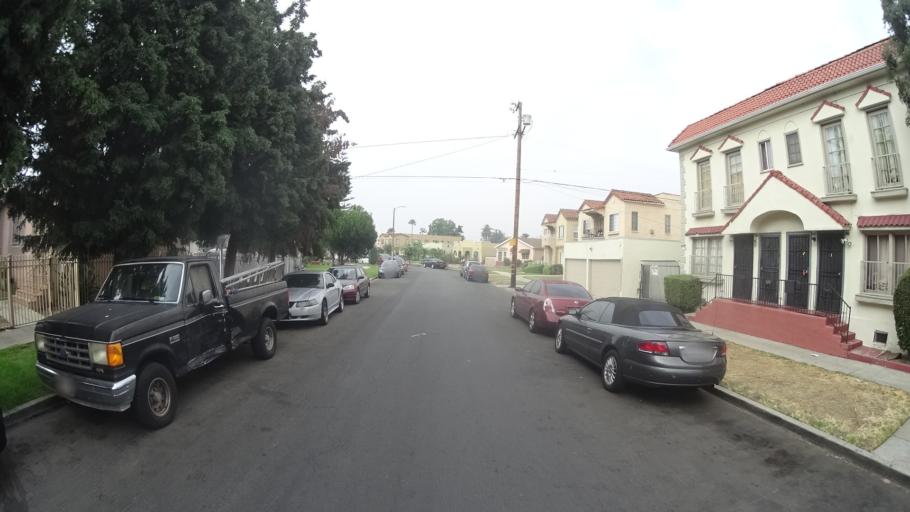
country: US
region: California
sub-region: Los Angeles County
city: View Park-Windsor Hills
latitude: 34.0296
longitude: -118.3291
